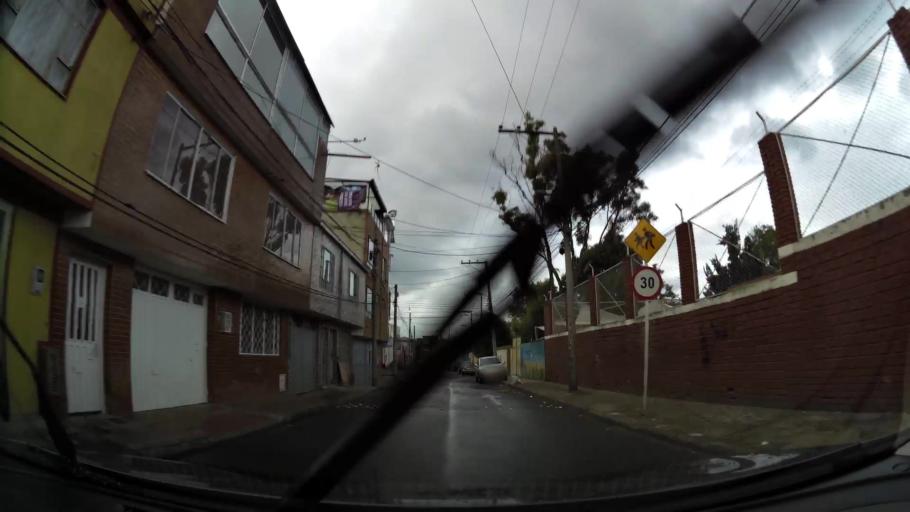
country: CO
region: Bogota D.C.
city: Barrio San Luis
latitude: 4.6726
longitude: -74.0786
